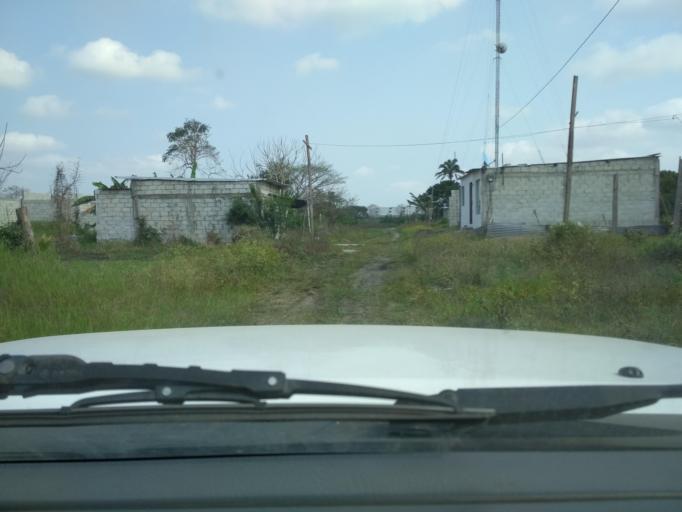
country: MX
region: Veracruz
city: El Tejar
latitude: 19.0842
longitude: -96.1666
